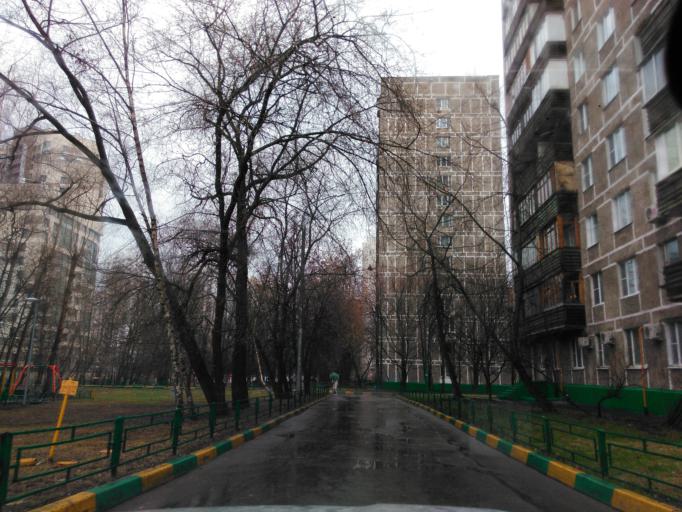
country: RU
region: Moskovskaya
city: Levoberezhnyy
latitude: 55.8664
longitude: 37.4694
